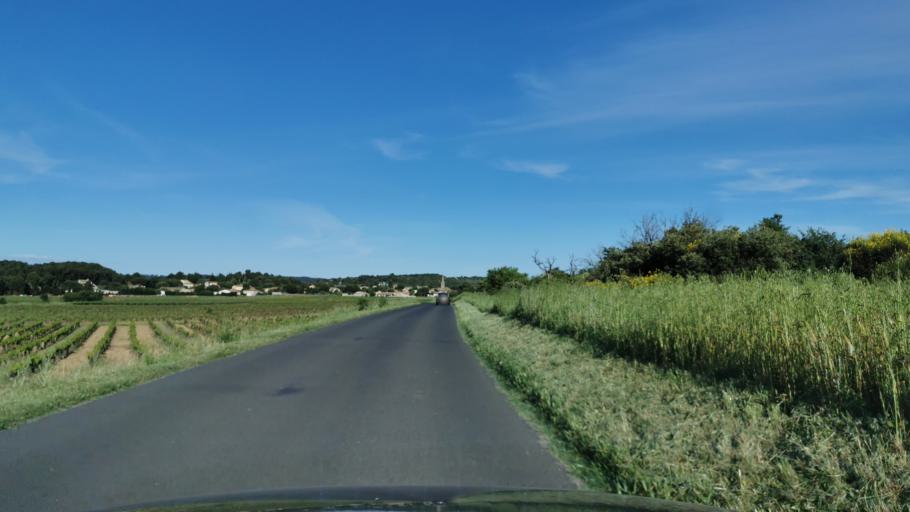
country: FR
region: Languedoc-Roussillon
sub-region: Departement de l'Aude
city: Nevian
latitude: 43.2138
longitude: 2.8899
